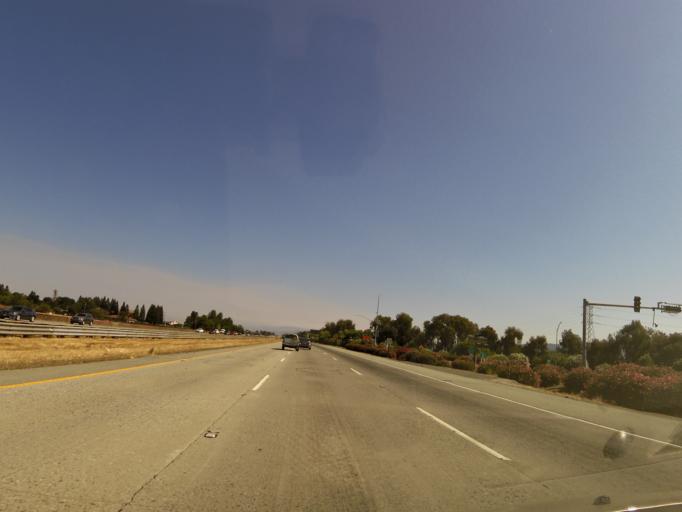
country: US
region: California
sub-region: Santa Clara County
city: Gilroy
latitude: 37.0403
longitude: -121.5764
